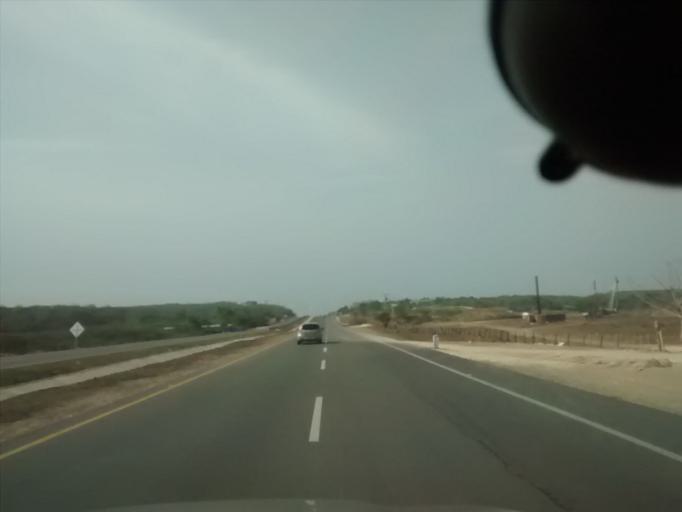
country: CO
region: Bolivar
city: Cartagena
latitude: 10.5045
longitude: -75.4736
